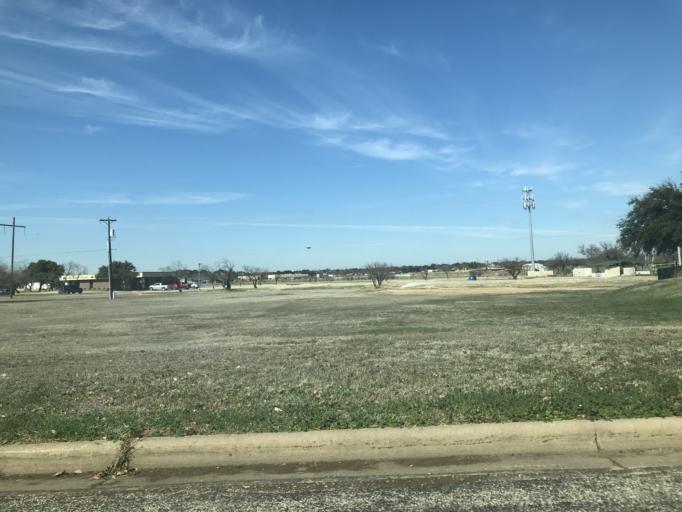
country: US
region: Texas
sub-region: Tom Green County
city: San Angelo
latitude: 31.4280
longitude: -100.4782
